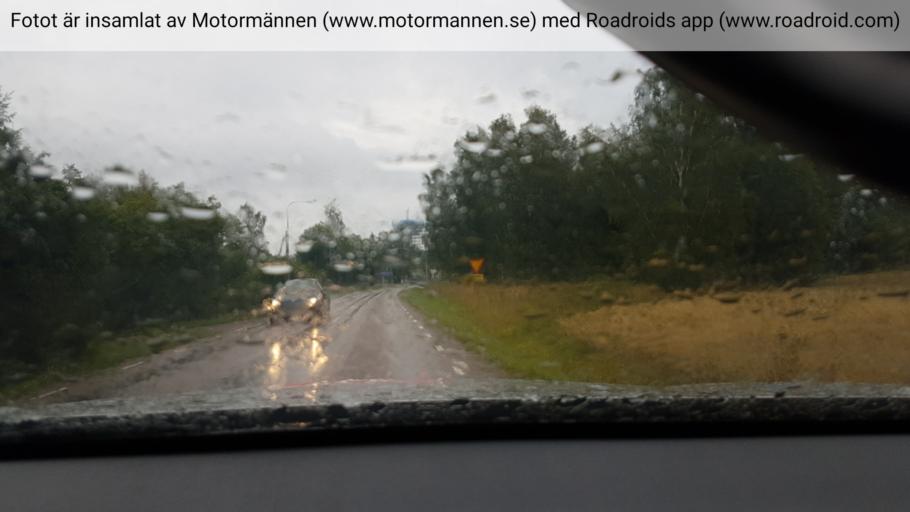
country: SE
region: Uppsala
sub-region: Tierps Kommun
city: Karlholmsbruk
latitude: 60.5193
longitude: 17.6074
